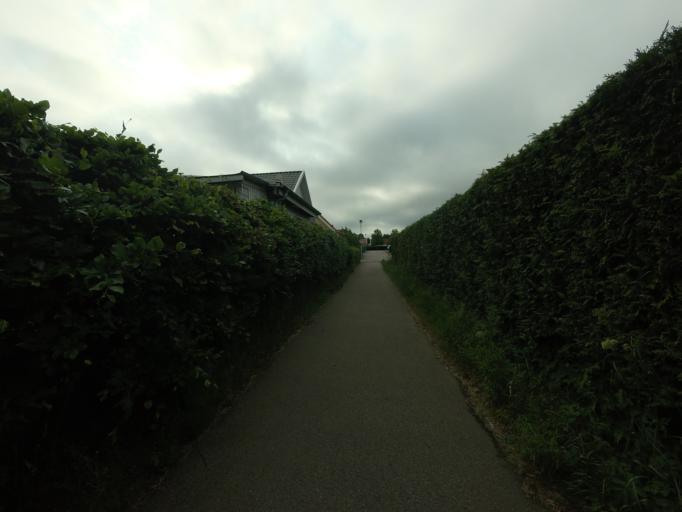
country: SE
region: Skane
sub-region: Bastads Kommun
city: Forslov
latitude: 56.3535
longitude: 12.8246
